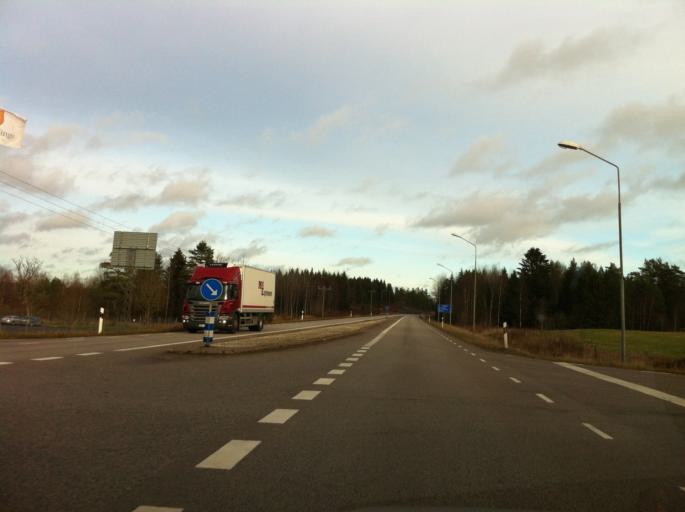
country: SE
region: Kronoberg
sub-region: Uppvidinge Kommun
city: Aseda
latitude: 57.1307
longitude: 15.2731
